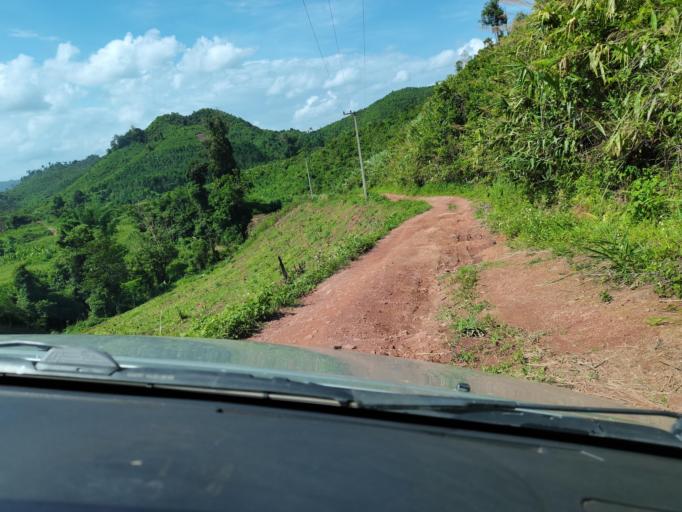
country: LA
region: Loungnamtha
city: Muang Nale
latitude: 20.5592
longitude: 101.0582
